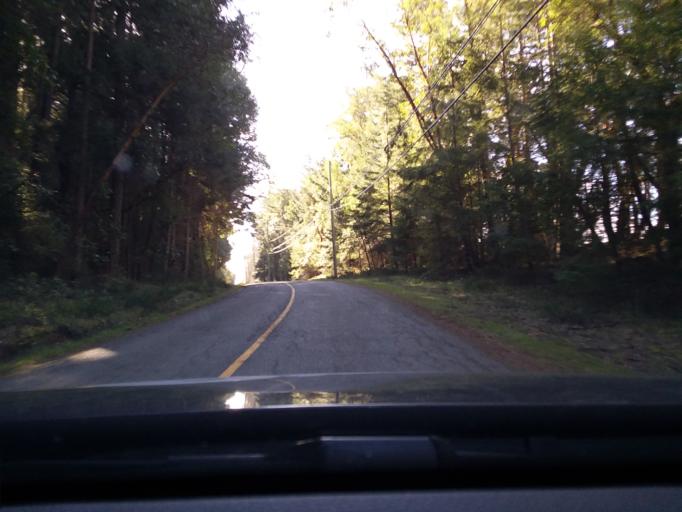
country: CA
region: British Columbia
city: North Cowichan
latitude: 48.9598
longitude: -123.5448
